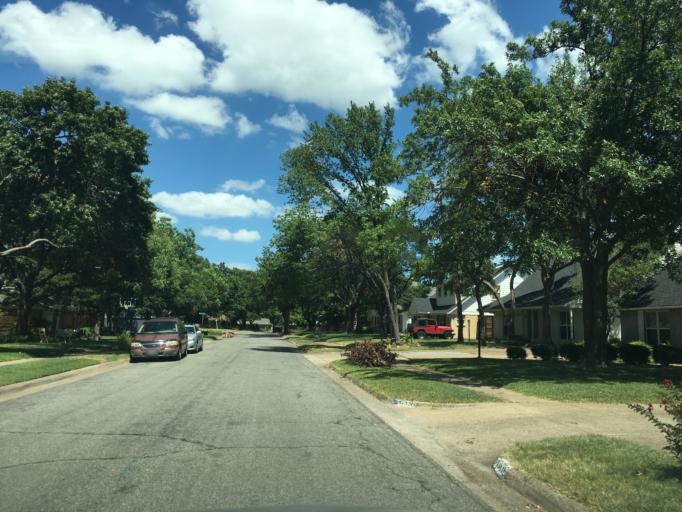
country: US
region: Texas
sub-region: Dallas County
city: Garland
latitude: 32.8485
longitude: -96.6960
